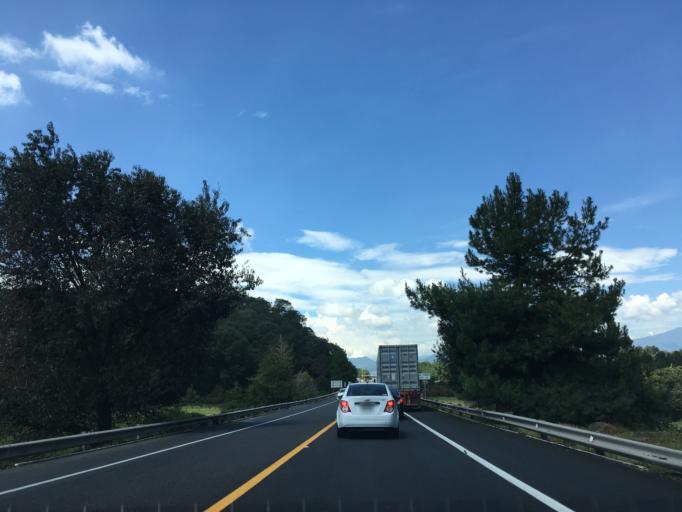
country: MX
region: Michoacan
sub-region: Patzcuaro
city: Santa Ana Chapitiro
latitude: 19.5042
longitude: -101.6525
